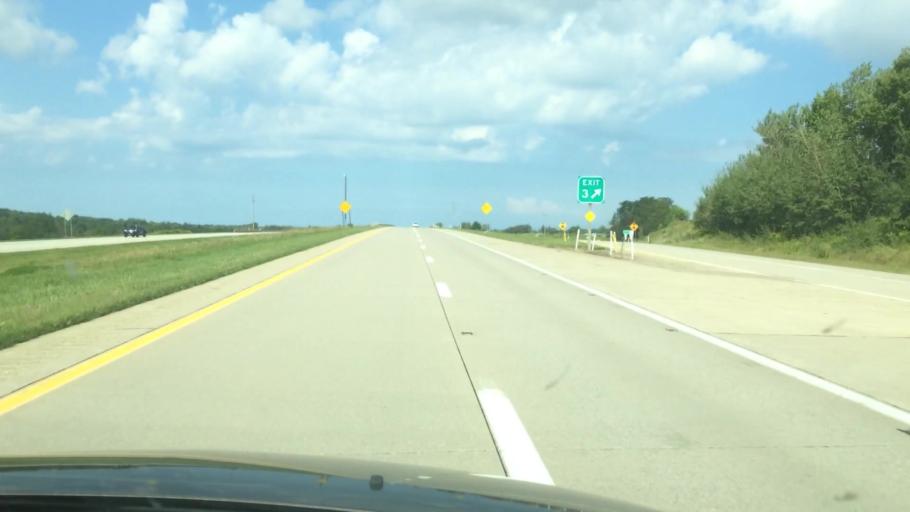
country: US
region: Pennsylvania
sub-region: Erie County
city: North East
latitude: 42.1362
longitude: -79.8187
